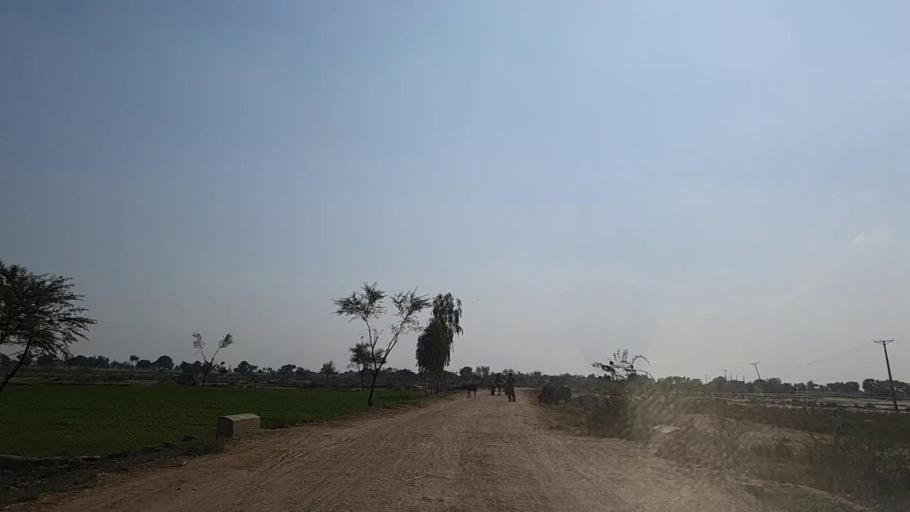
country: PK
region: Sindh
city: Daur
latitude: 26.4557
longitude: 68.2502
